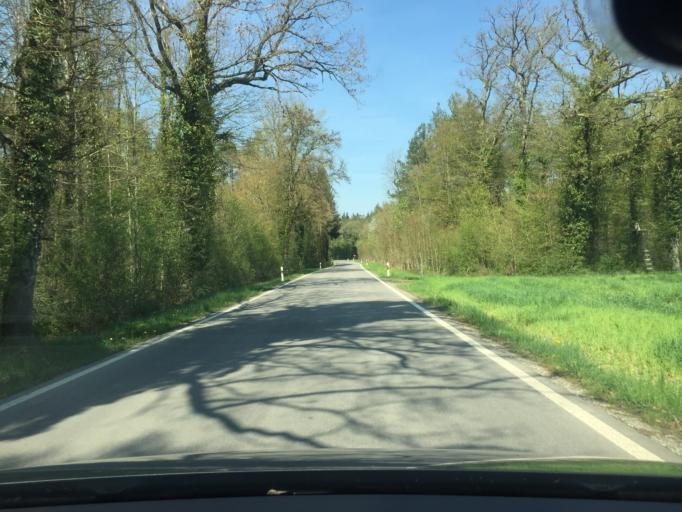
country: CH
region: Zurich
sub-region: Bezirk Andelfingen
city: Marthalen
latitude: 47.6194
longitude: 8.6287
